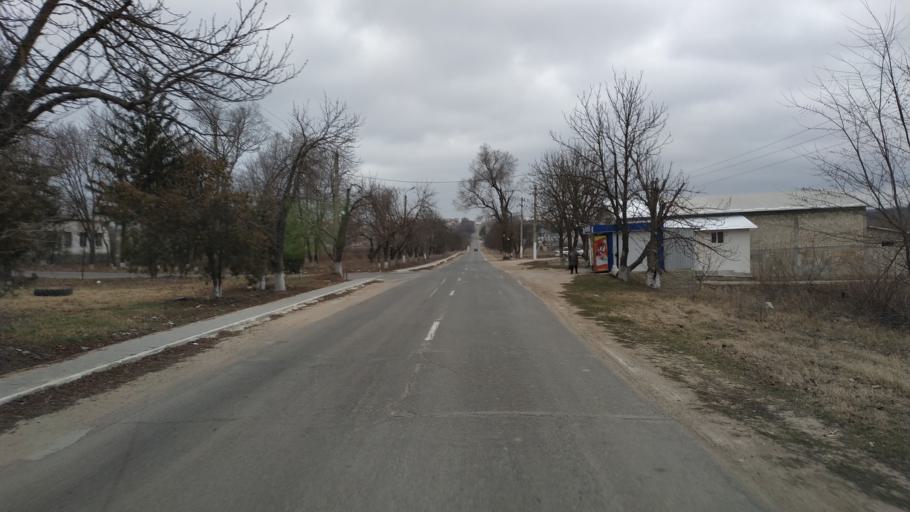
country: MD
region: Laloveni
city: Ialoveni
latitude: 46.9102
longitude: 28.8095
